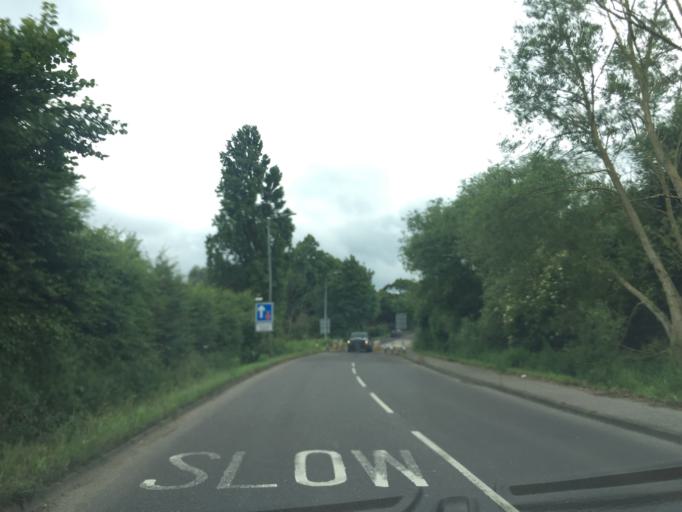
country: GB
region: England
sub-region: Greater London
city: Collier Row
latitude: 51.6247
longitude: 0.1897
